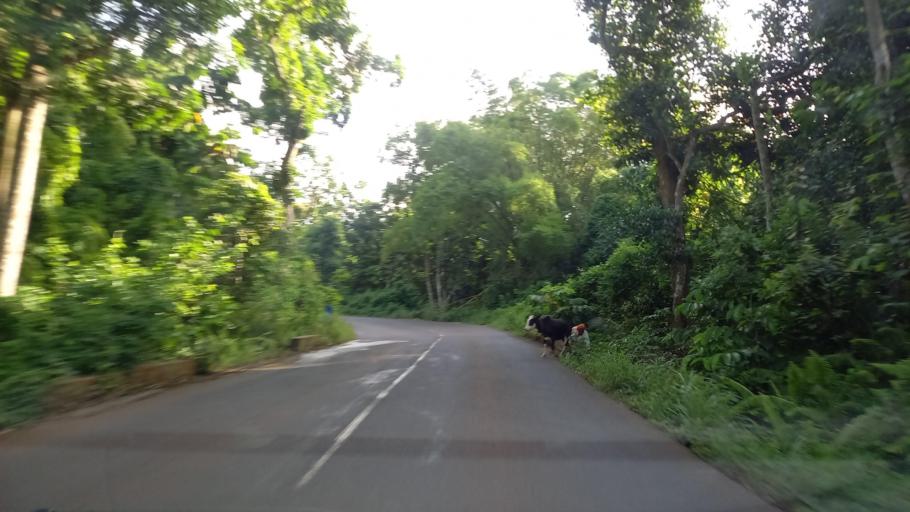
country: YT
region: Bandraboua
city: Bandraboua
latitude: -12.7341
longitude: 45.1189
